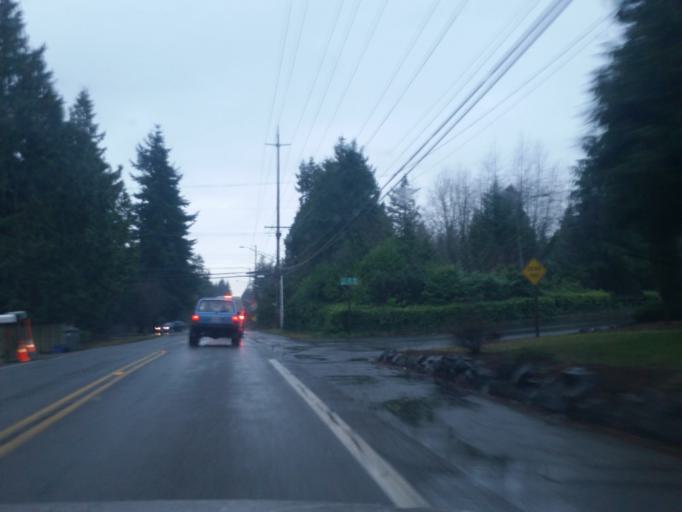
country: US
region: Washington
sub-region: Snohomish County
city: Meadowdale
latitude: 47.8716
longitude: -122.3024
